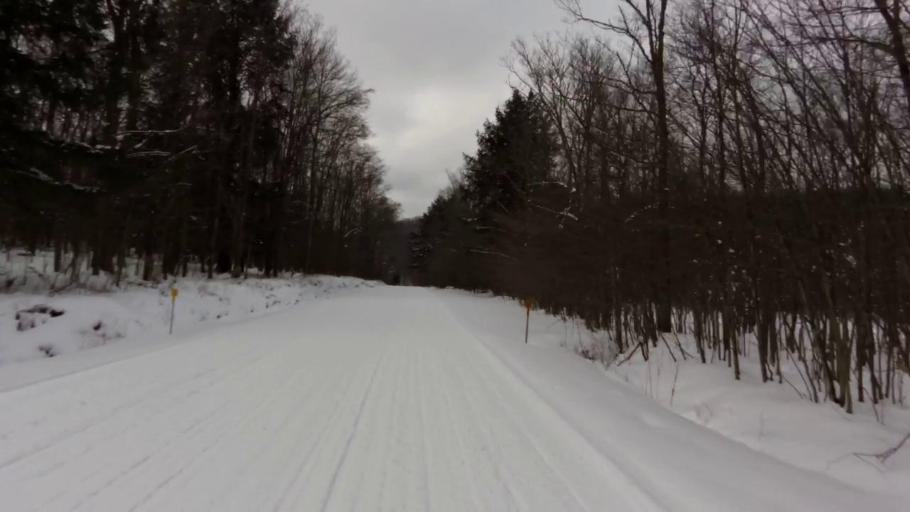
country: US
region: New York
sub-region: Cattaraugus County
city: Salamanca
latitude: 42.0335
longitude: -78.8041
